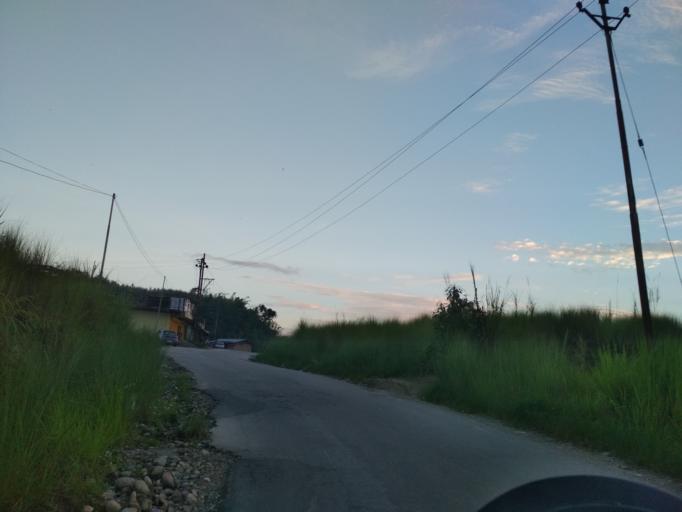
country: IN
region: Arunachal Pradesh
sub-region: Papum Pare
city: Naharlagun
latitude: 27.0974
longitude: 93.6675
